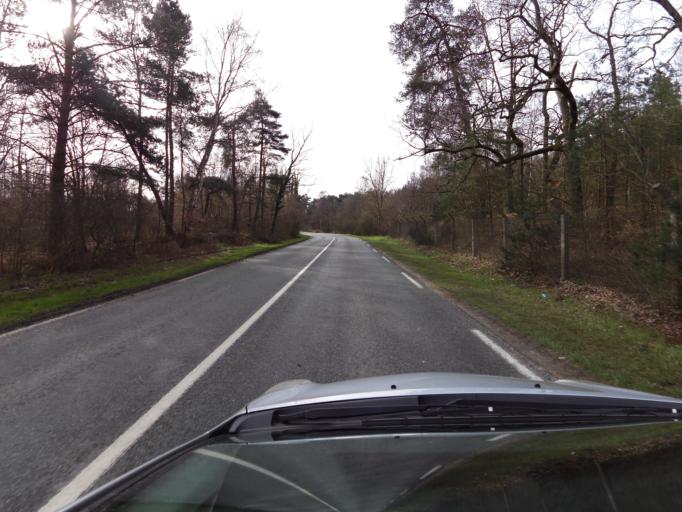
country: FR
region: Picardie
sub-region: Departement de l'Oise
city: Ver-sur-Launette
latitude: 49.1425
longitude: 2.6832
